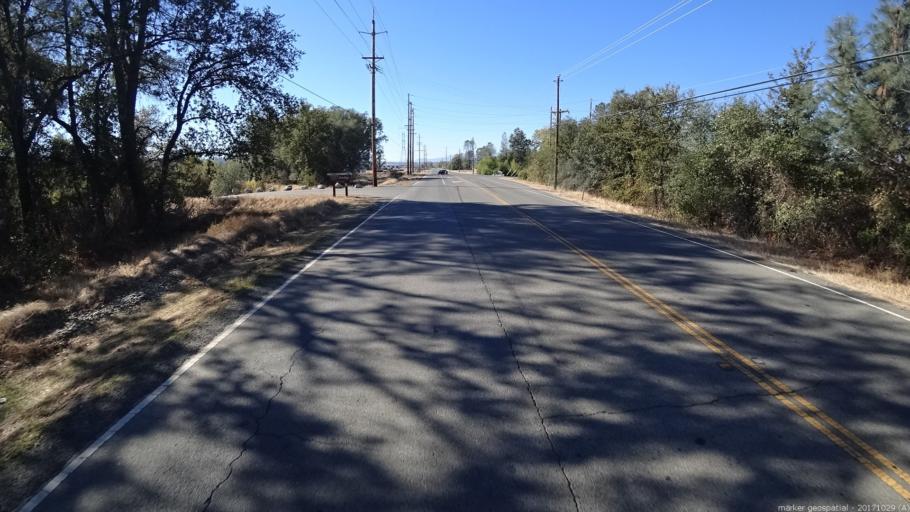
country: US
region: California
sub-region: Shasta County
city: Redding
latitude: 40.5033
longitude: -122.4220
